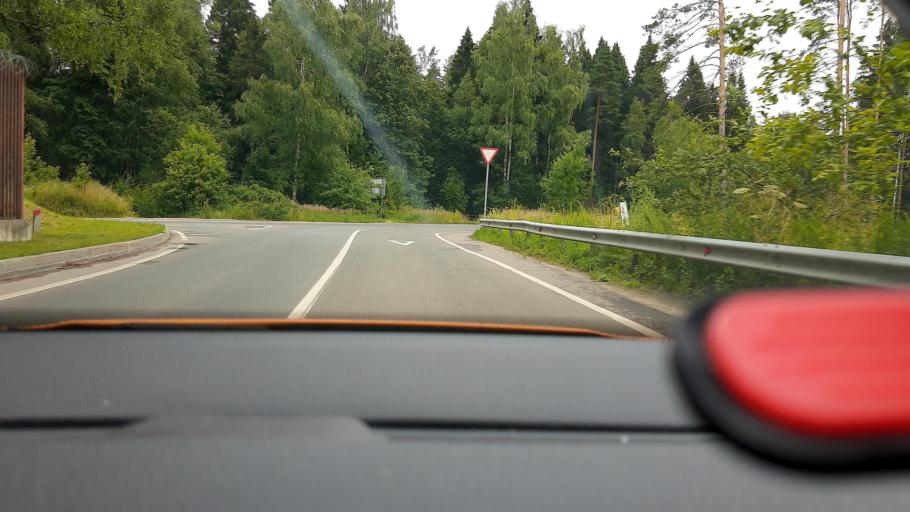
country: RU
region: Moskovskaya
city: Pirogovskiy
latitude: 55.9970
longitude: 37.6755
